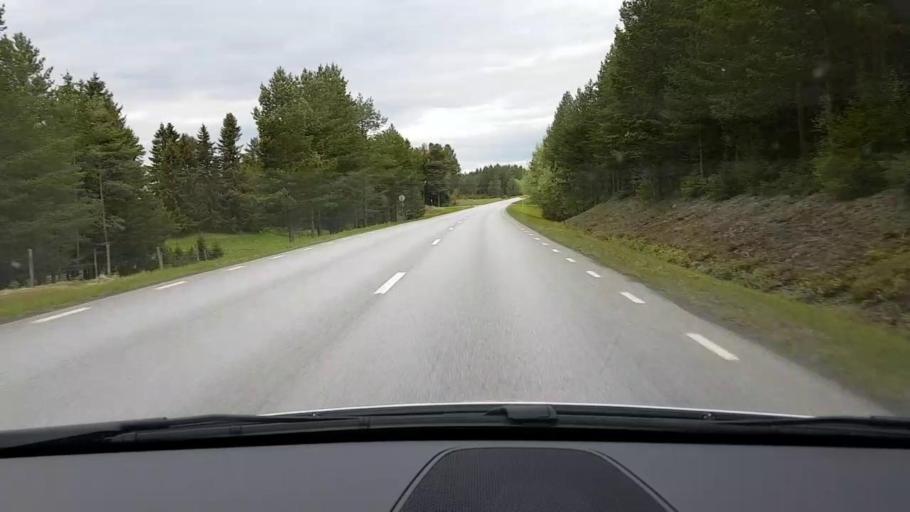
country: SE
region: Jaemtland
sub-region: Krokoms Kommun
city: Valla
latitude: 63.2740
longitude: 13.9448
